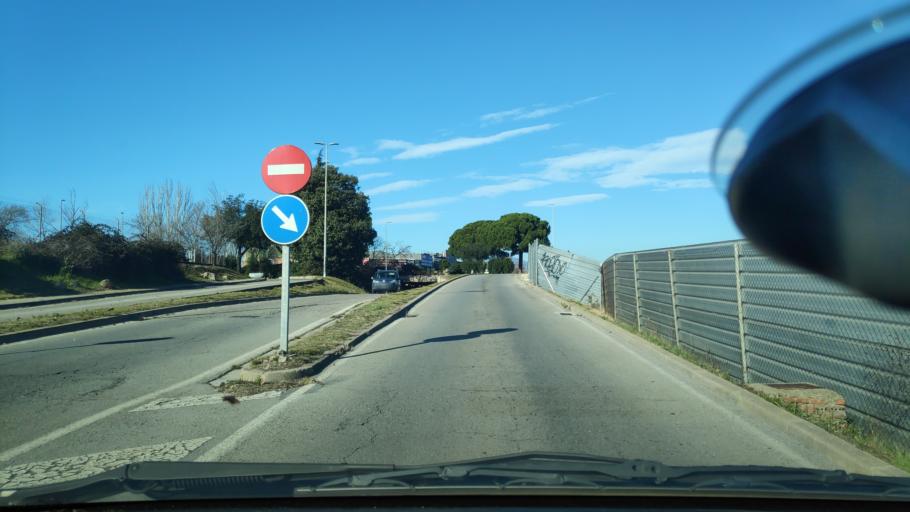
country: ES
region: Catalonia
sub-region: Provincia de Barcelona
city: Sabadell
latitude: 41.5268
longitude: 2.1053
